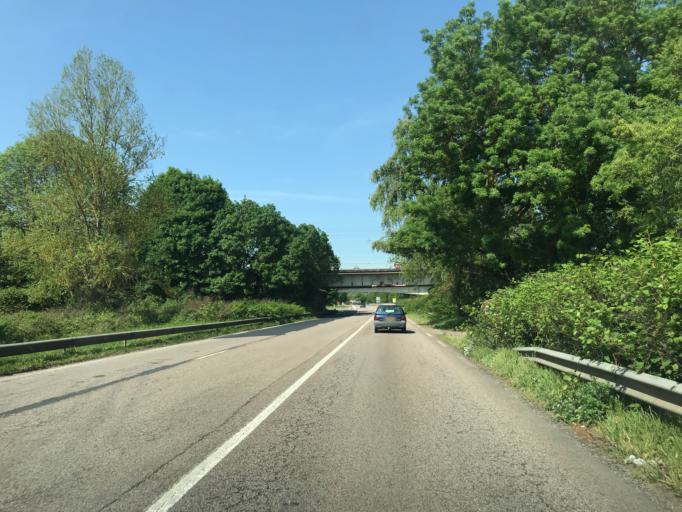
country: FR
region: Haute-Normandie
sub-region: Departement de la Seine-Maritime
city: Tourville-la-Riviere
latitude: 49.3343
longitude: 1.1045
